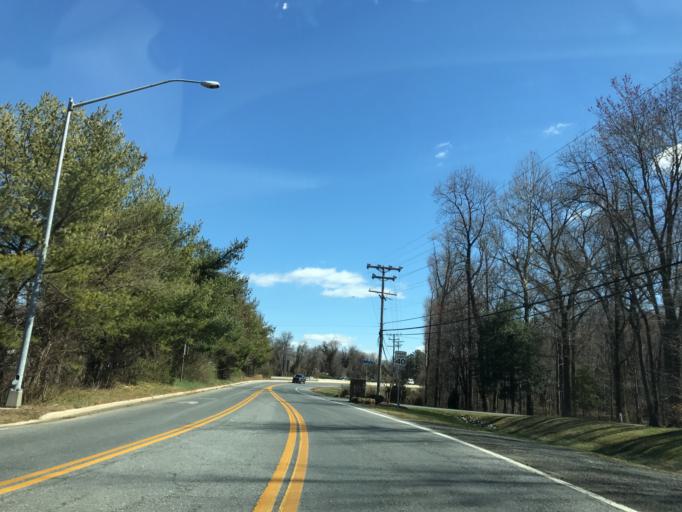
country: US
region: Maryland
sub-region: Anne Arundel County
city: Cape Saint Claire
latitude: 39.0250
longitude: -76.4393
